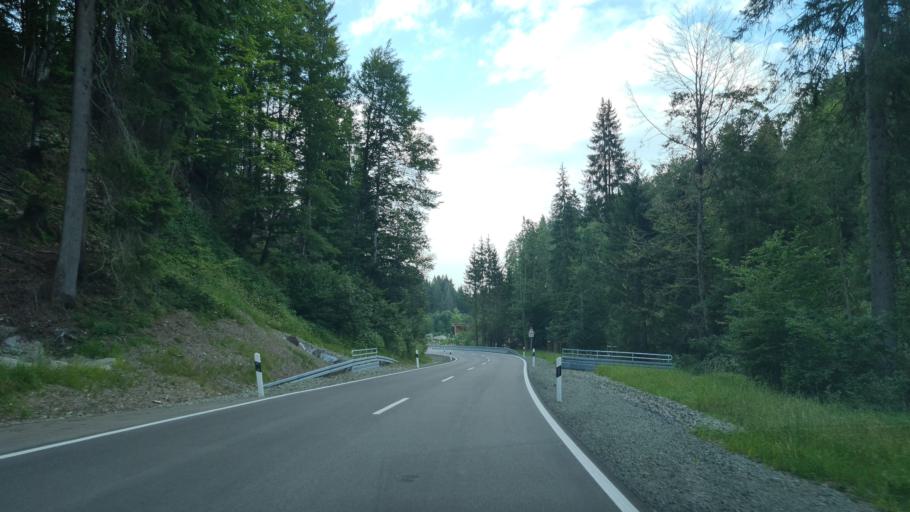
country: DE
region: Bavaria
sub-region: Swabia
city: Obermaiselstein
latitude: 47.4431
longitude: 10.2297
